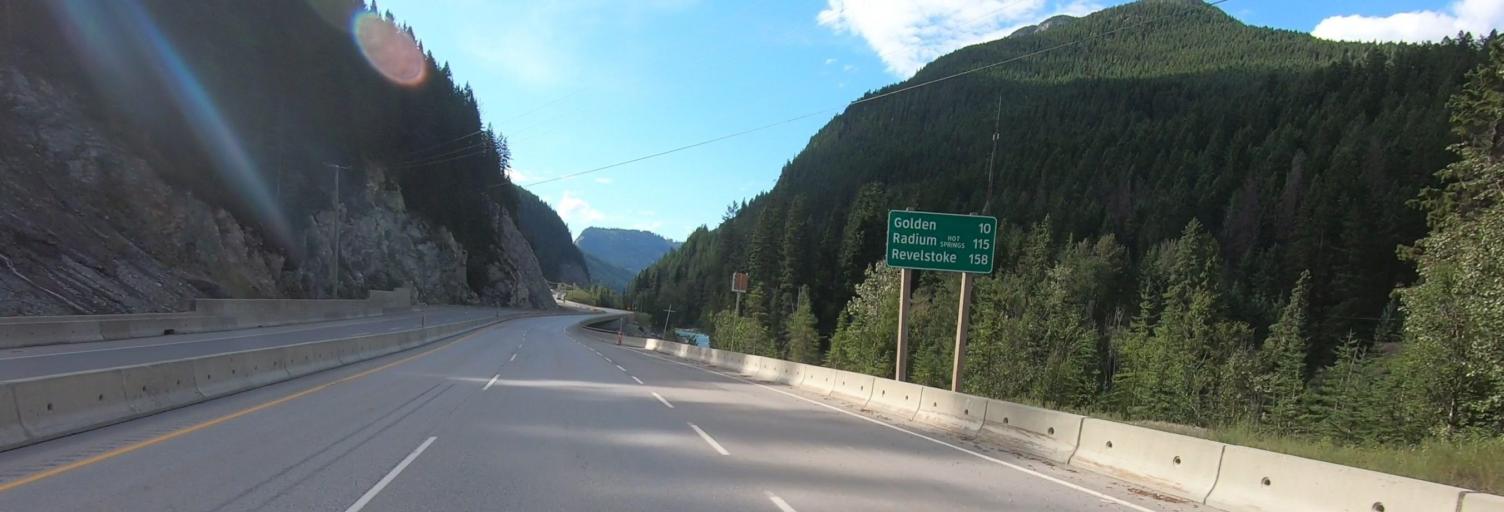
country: CA
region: British Columbia
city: Golden
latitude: 51.2883
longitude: -116.8274
